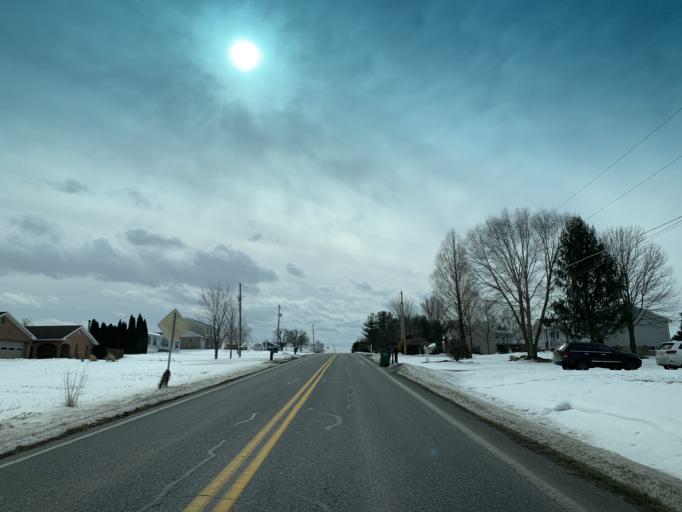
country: US
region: Pennsylvania
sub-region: York County
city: Red Lion
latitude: 39.8347
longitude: -76.6203
